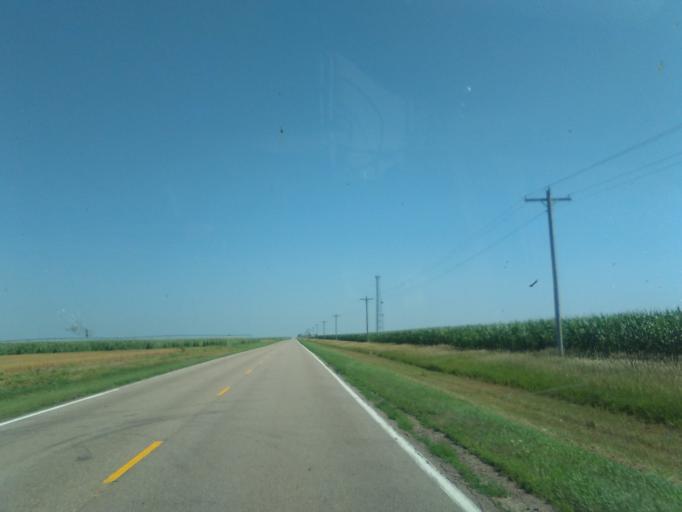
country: US
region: Kansas
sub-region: Cheyenne County
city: Saint Francis
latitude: 39.7728
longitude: -101.5420
